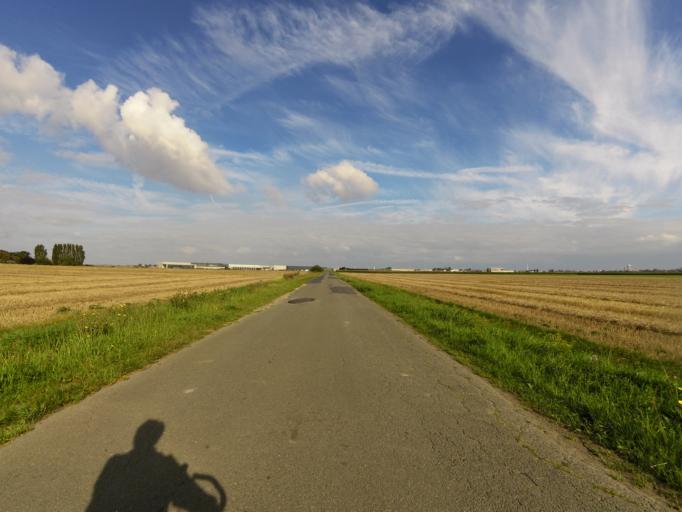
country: BE
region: Flanders
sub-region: Provincie West-Vlaanderen
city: Ostend
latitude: 51.1867
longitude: 2.9055
